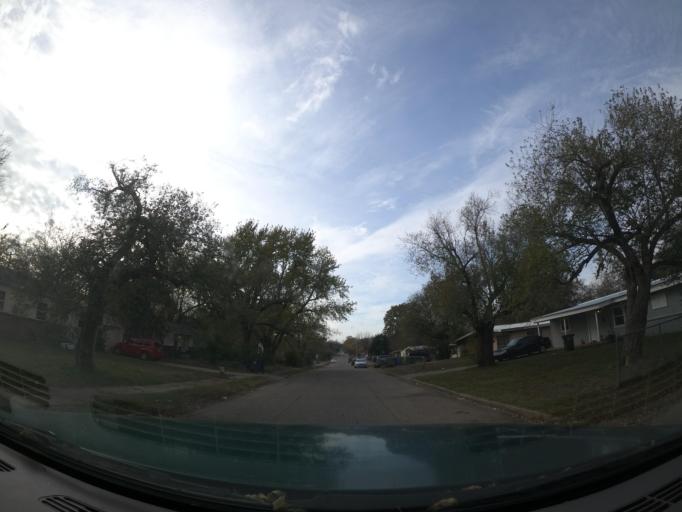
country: US
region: Oklahoma
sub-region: Tulsa County
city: Turley
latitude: 36.2314
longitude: -95.9869
